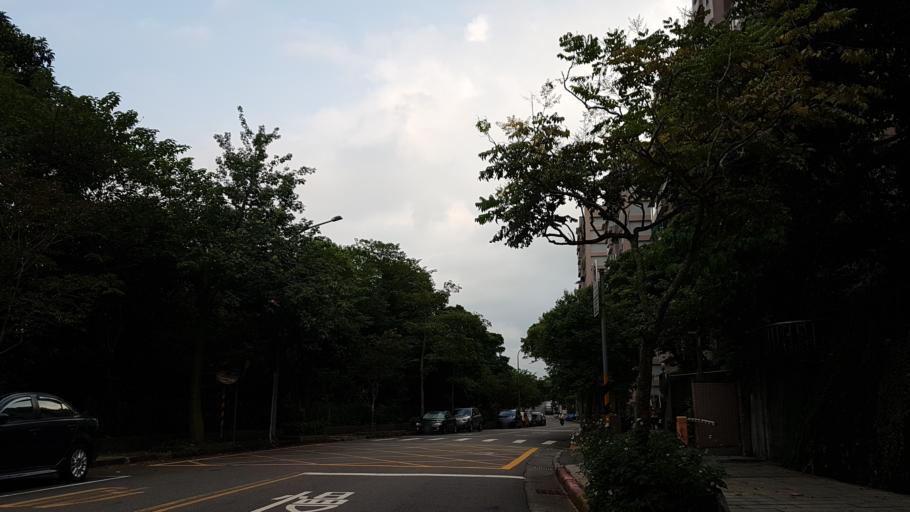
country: TW
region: Taipei
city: Taipei
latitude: 25.0045
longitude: 121.5690
